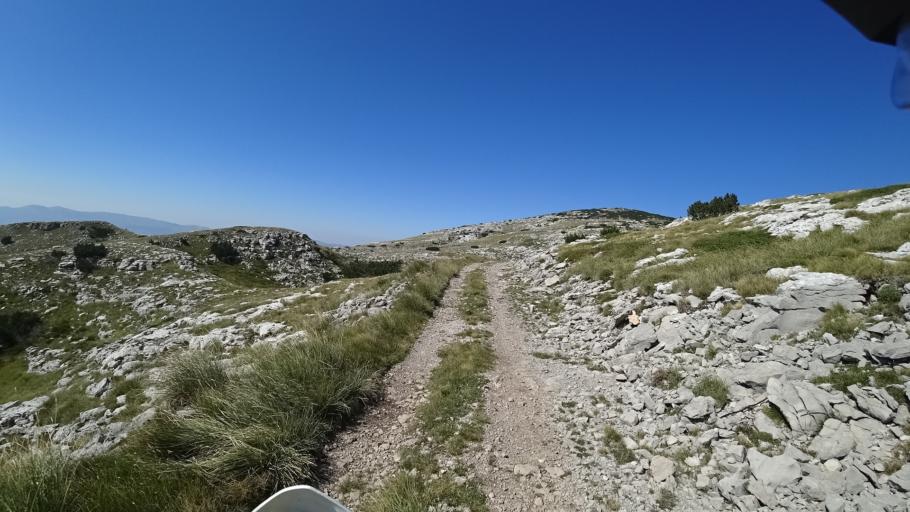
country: HR
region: Splitsko-Dalmatinska
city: Hrvace
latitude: 43.9309
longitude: 16.6027
